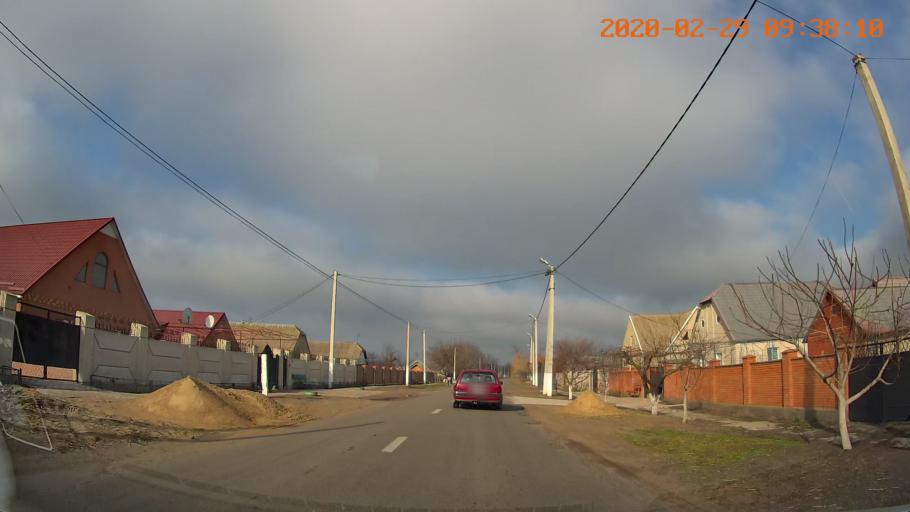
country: MD
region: Telenesti
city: Dnestrovsc
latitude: 46.6298
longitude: 29.8698
